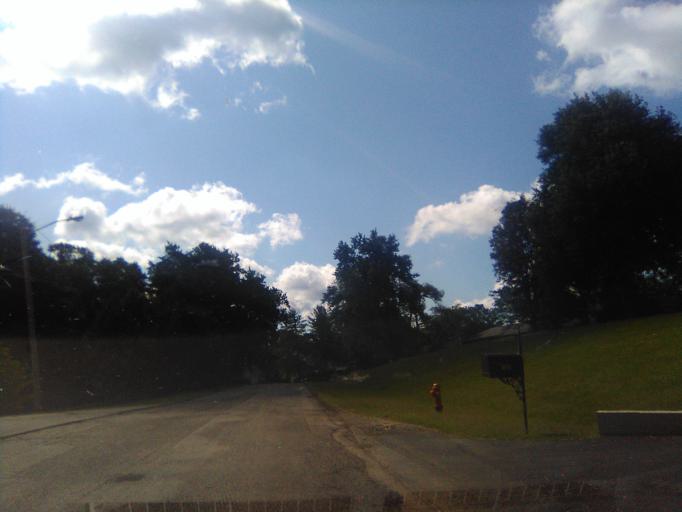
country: US
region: Tennessee
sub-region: Davidson County
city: Belle Meade
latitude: 36.1080
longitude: -86.8699
